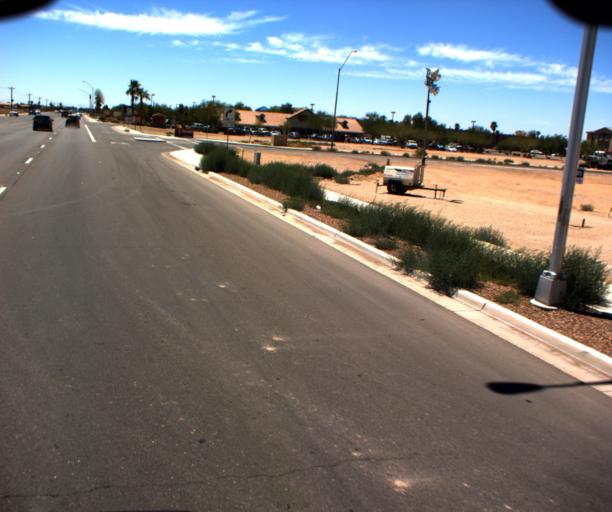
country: US
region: Arizona
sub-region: Pinal County
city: Casa Grande
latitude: 32.8797
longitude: -111.6960
